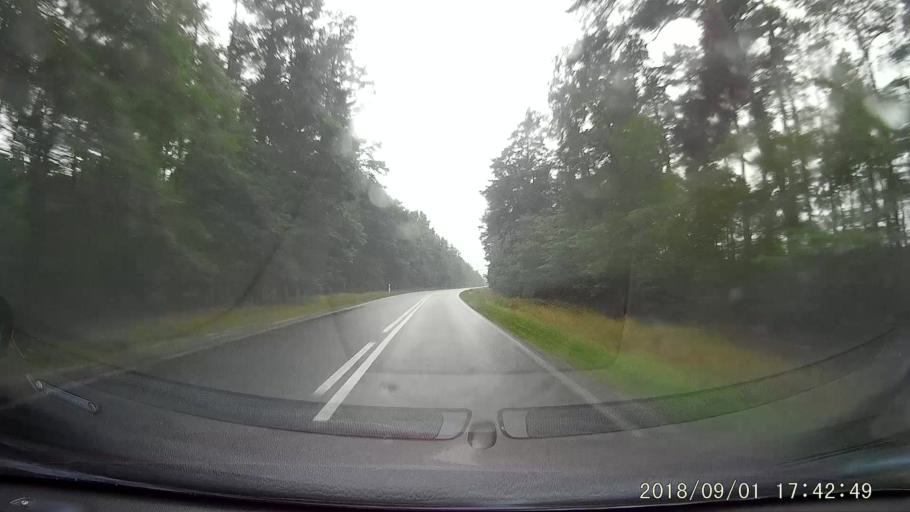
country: PL
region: Lubusz
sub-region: Powiat zaganski
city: Ilowa
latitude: 51.5516
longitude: 15.2563
